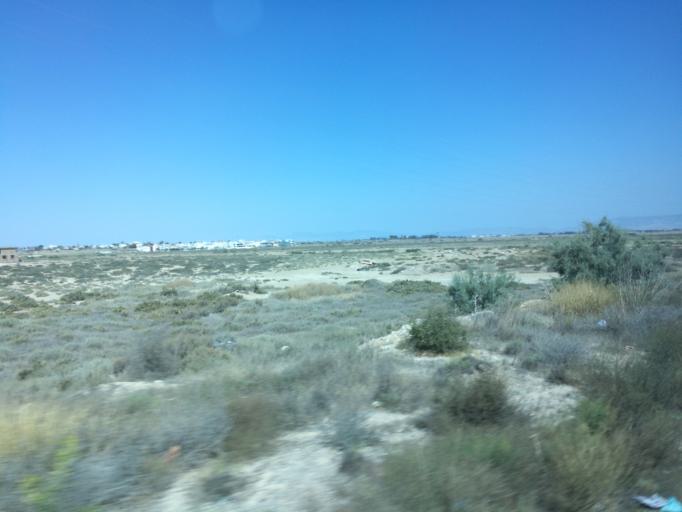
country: CY
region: Ammochostos
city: Famagusta
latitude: 35.1639
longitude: 33.8992
